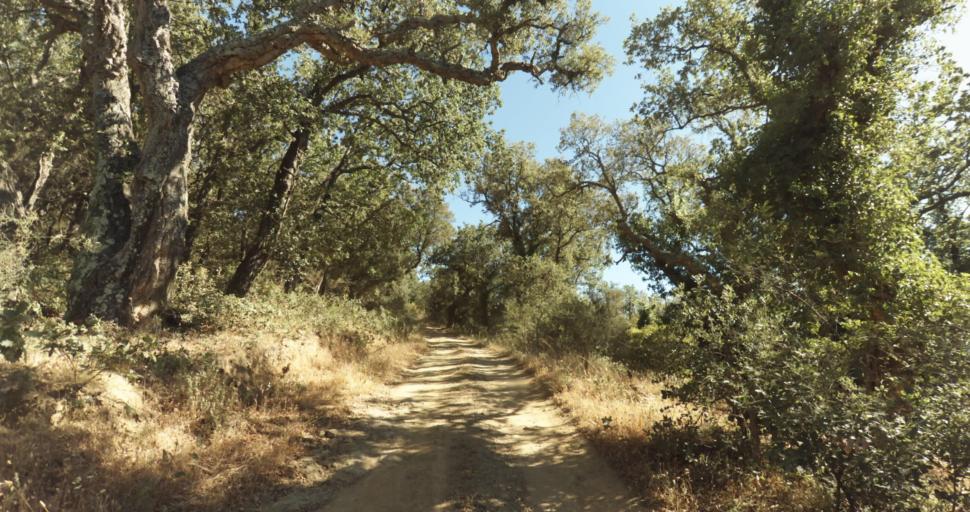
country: FR
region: Provence-Alpes-Cote d'Azur
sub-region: Departement du Var
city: Gassin
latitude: 43.2419
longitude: 6.5837
